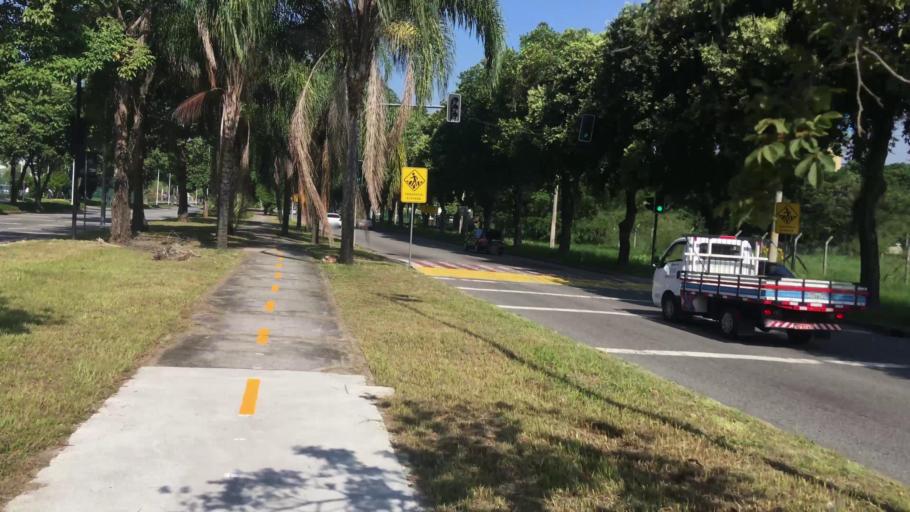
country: BR
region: Rio de Janeiro
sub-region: Rio De Janeiro
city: Rio de Janeiro
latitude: -22.8470
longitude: -43.2358
